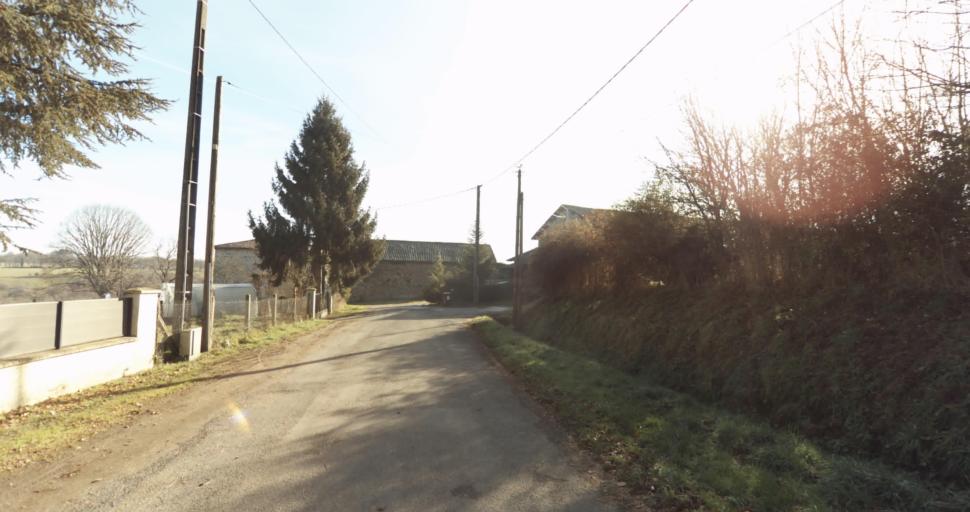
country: FR
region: Limousin
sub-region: Departement de la Haute-Vienne
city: Aixe-sur-Vienne
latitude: 45.7830
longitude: 1.1292
